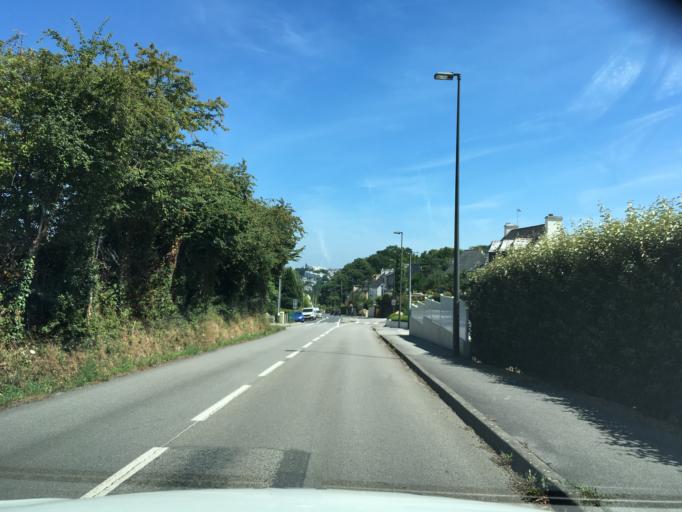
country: FR
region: Brittany
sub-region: Departement du Finistere
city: Quimper
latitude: 48.0042
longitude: -4.1256
